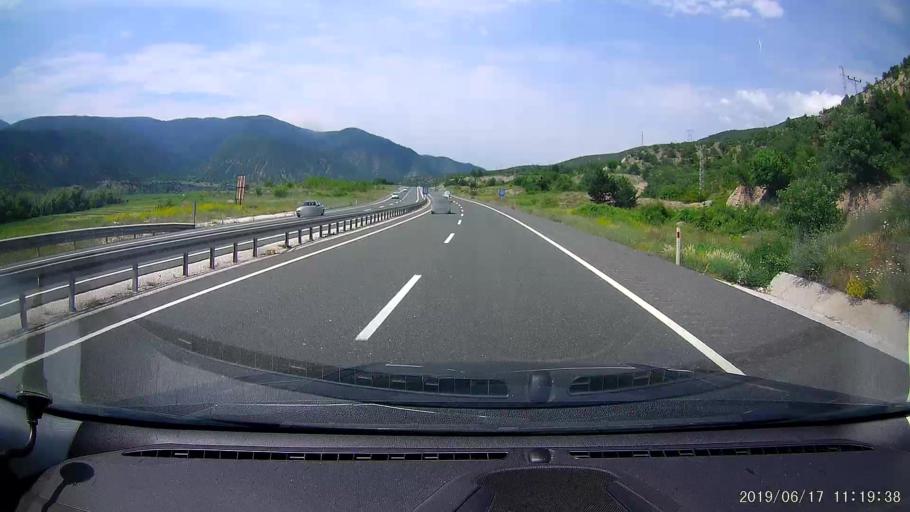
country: TR
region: Cankiri
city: Yaprakli
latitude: 40.9242
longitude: 33.8233
